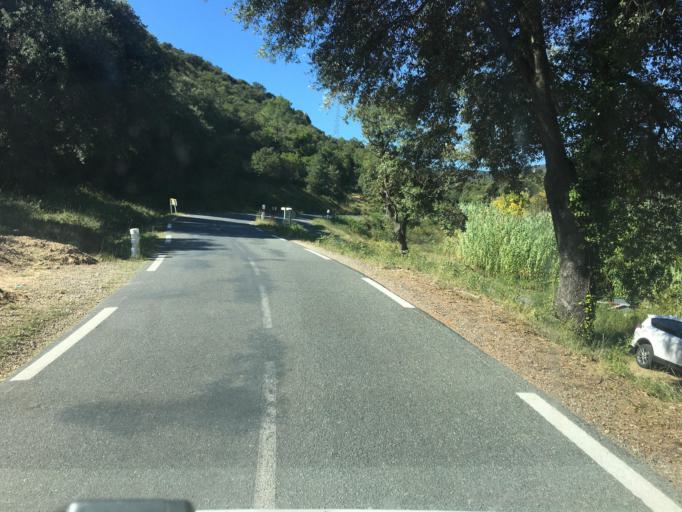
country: FR
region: Languedoc-Roussillon
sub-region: Departement de l'Herault
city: Nebian
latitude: 43.6166
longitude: 3.3673
